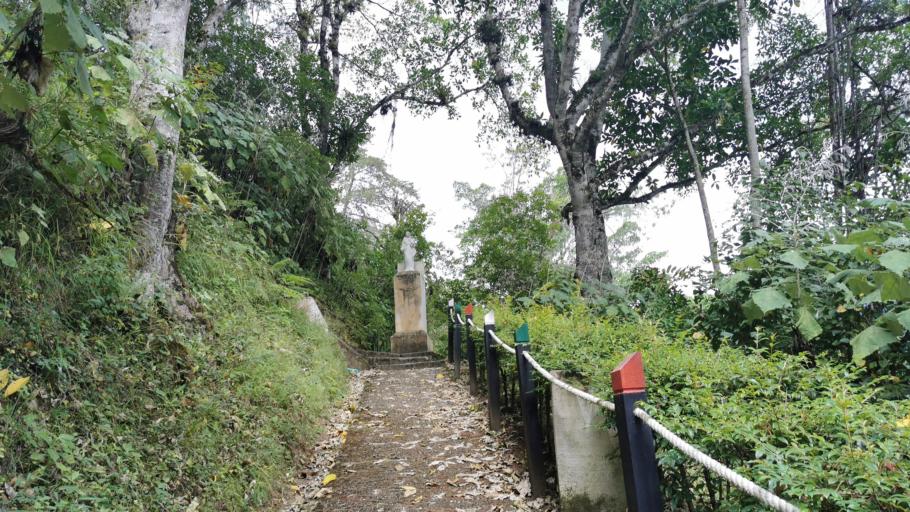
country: CO
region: Cundinamarca
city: Tenza
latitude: 5.0751
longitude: -73.4201
